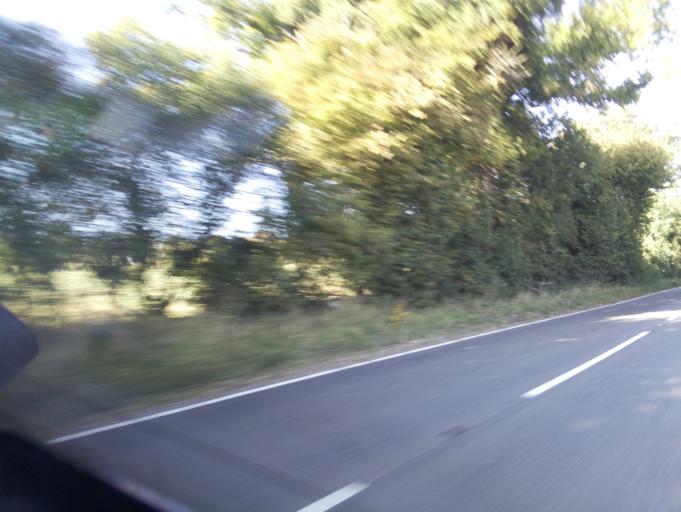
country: GB
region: England
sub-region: Hampshire
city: Four Marks
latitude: 51.0397
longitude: -1.0678
